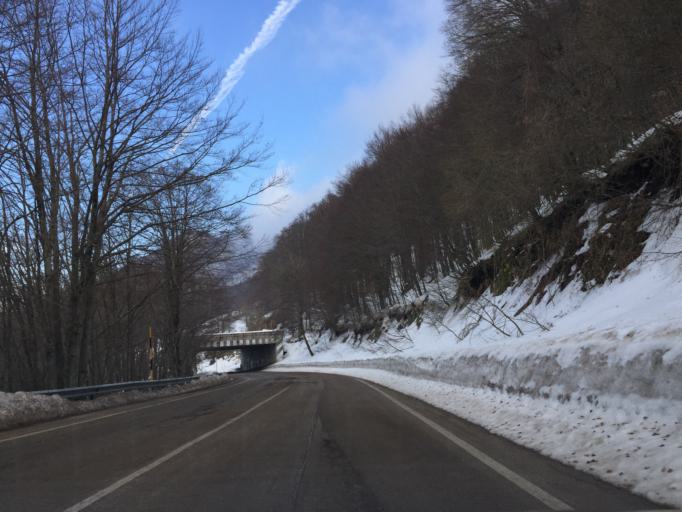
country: IT
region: Molise
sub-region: Provincia di Campobasso
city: San Massimo
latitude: 41.4661
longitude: 14.4095
